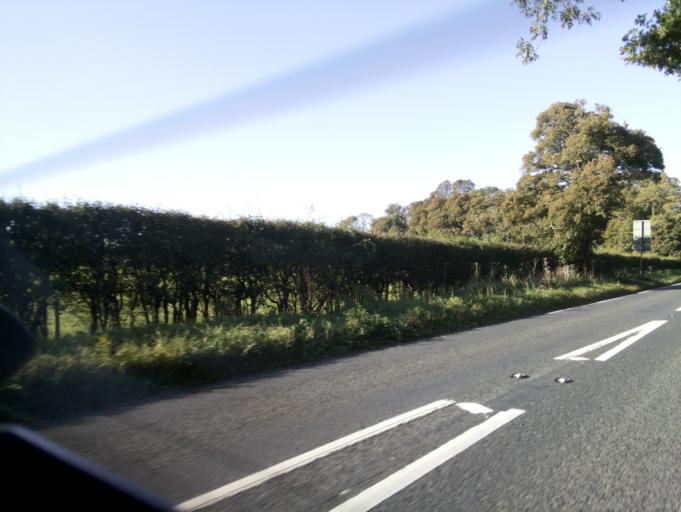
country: GB
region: England
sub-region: Hampshire
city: Swanmore
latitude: 50.9942
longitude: -1.1185
